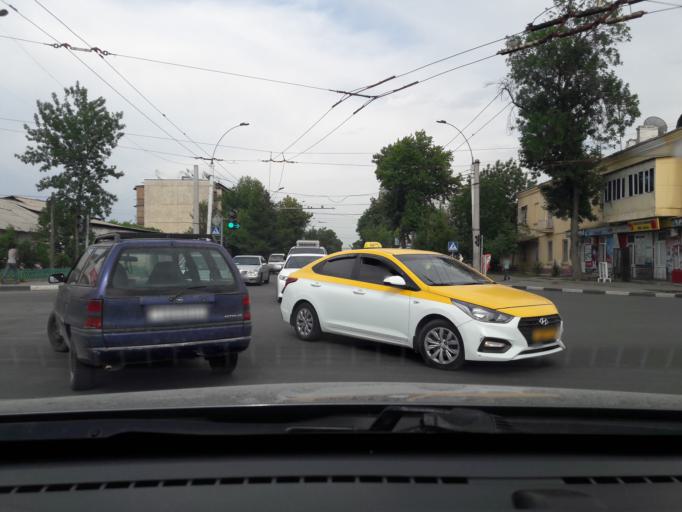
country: TJ
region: Dushanbe
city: Dushanbe
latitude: 38.5461
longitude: 68.7552
